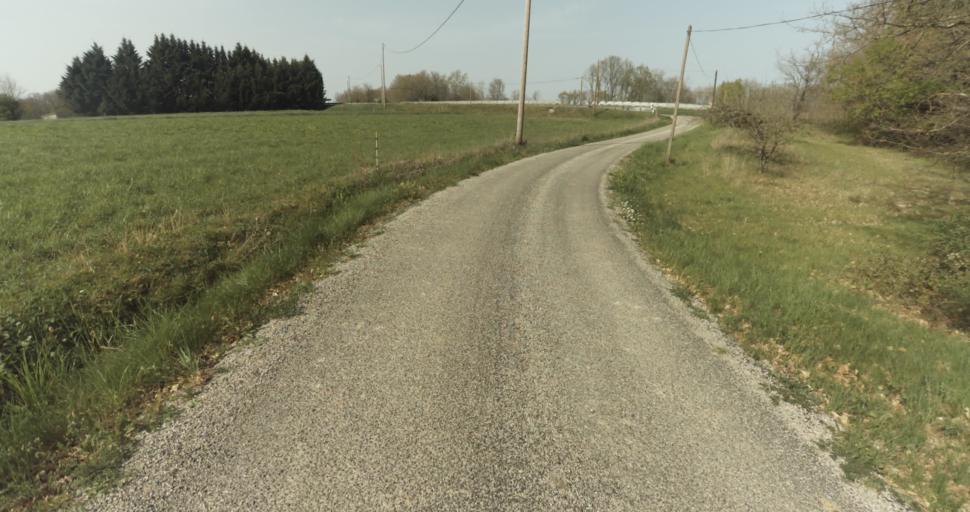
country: FR
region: Midi-Pyrenees
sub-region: Departement du Tarn-et-Garonne
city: Cazes-Mondenard
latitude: 44.1586
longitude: 1.1694
